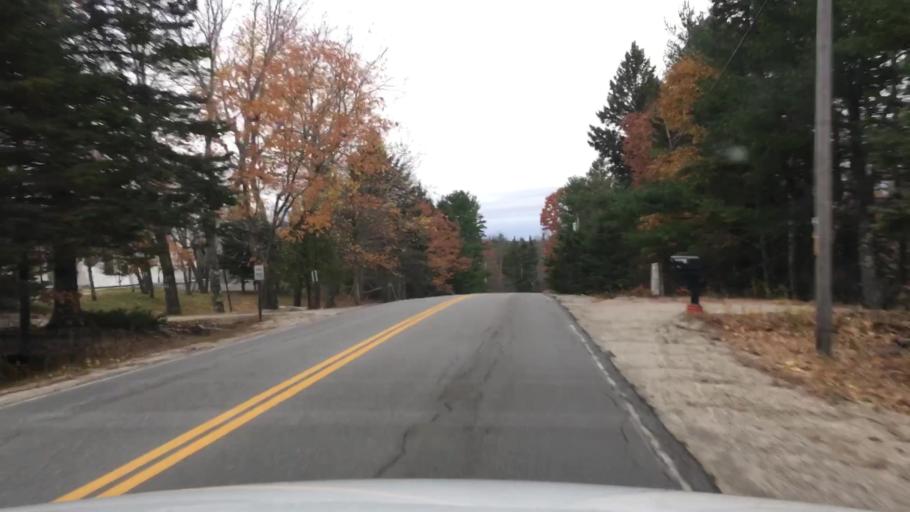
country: US
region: Maine
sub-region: Hancock County
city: Penobscot
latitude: 44.4307
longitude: -68.6274
